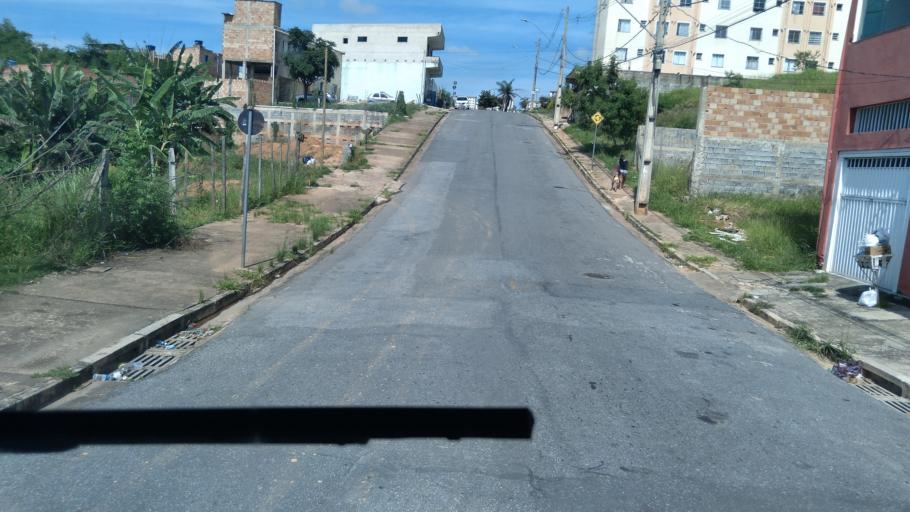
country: BR
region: Minas Gerais
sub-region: Santa Luzia
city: Santa Luzia
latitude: -19.8423
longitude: -43.8826
